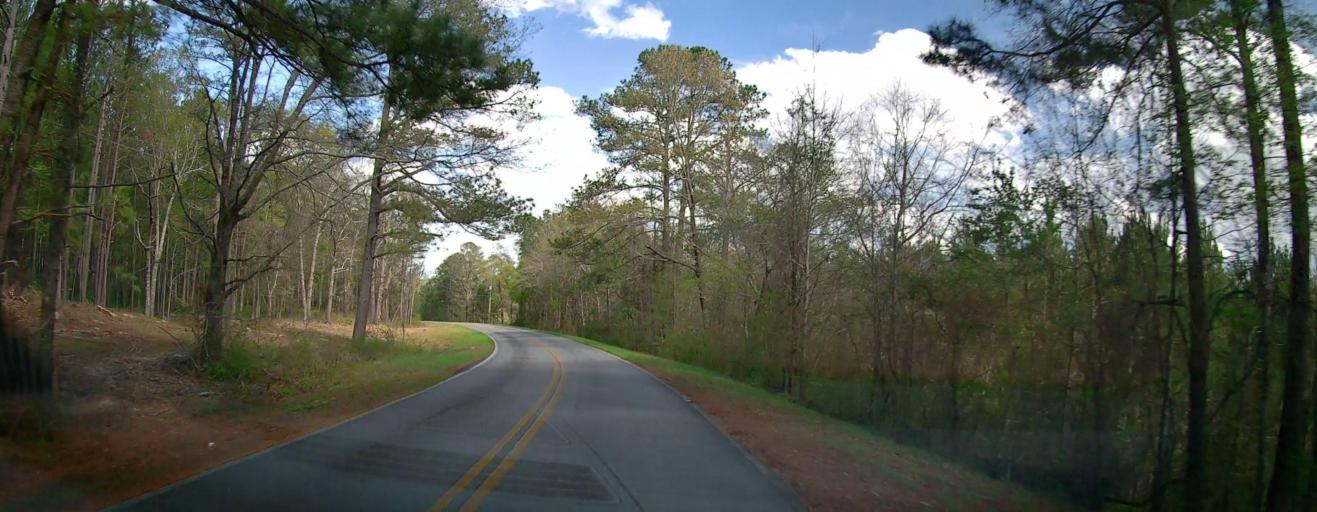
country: US
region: Georgia
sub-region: Wilkinson County
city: Gordon
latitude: 32.8012
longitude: -83.4229
